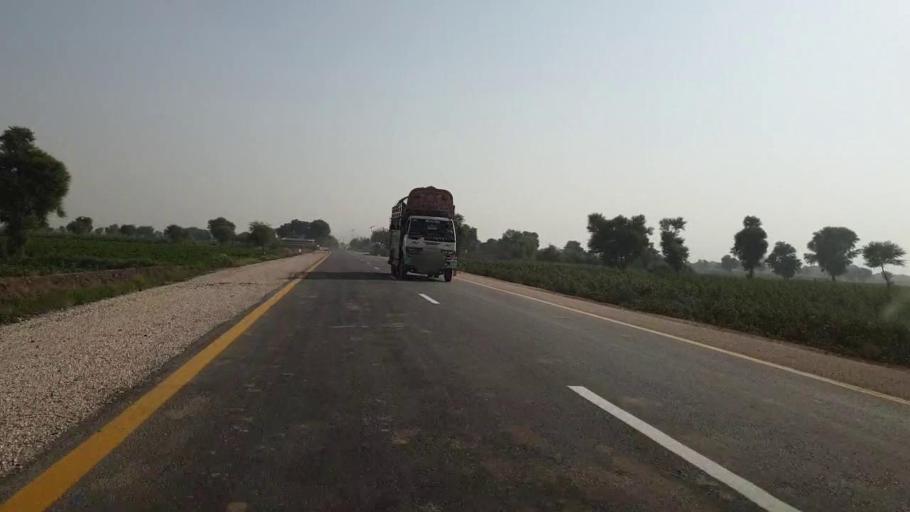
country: PK
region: Sindh
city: Bhan
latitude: 26.5380
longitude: 67.7880
